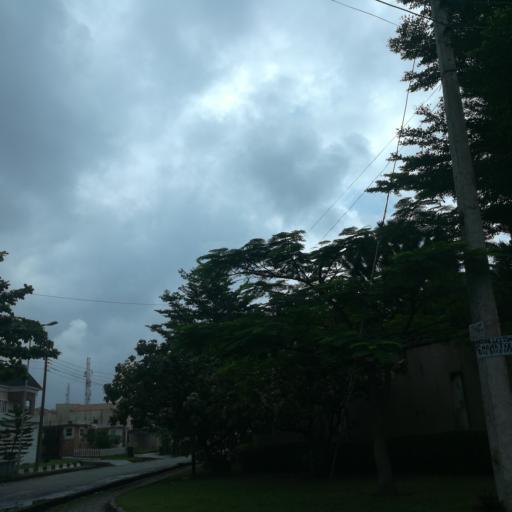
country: NG
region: Lagos
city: Ikoyi
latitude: 6.4397
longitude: 3.4584
